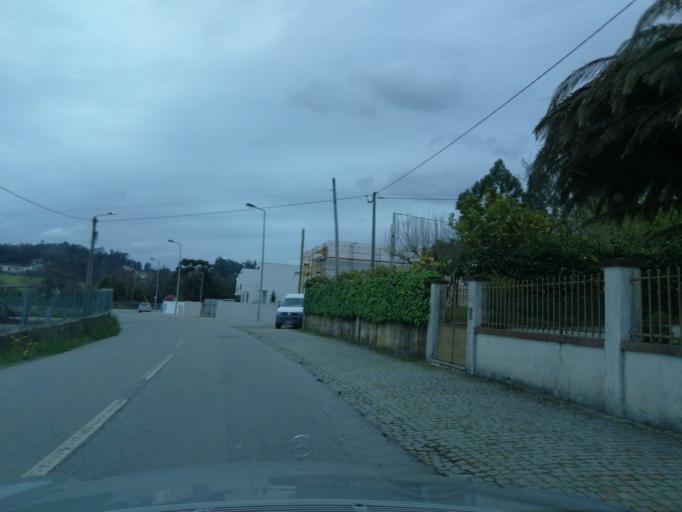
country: PT
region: Braga
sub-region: Braga
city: Oliveira
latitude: 41.4810
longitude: -8.4712
